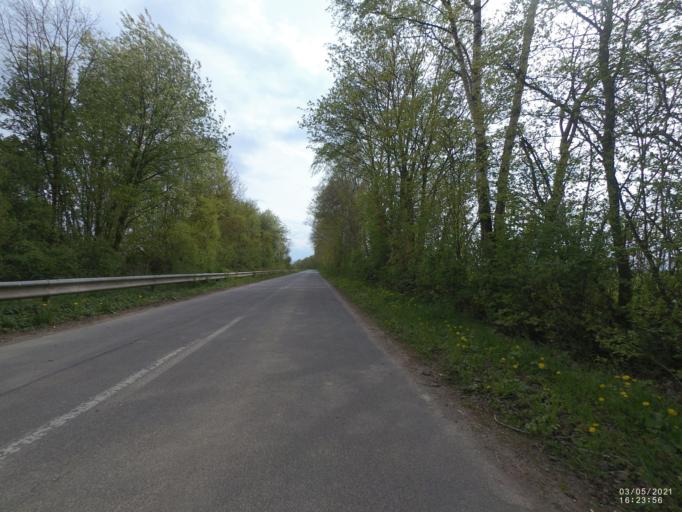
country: DE
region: Rheinland-Pfalz
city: Lonnig
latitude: 50.3363
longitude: 7.4215
